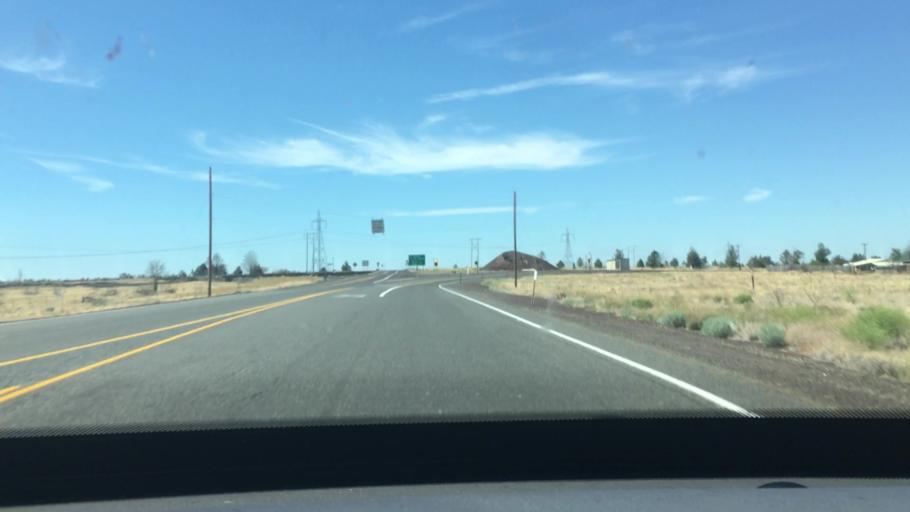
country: US
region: Oregon
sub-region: Jefferson County
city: Madras
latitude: 44.9188
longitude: -120.9447
